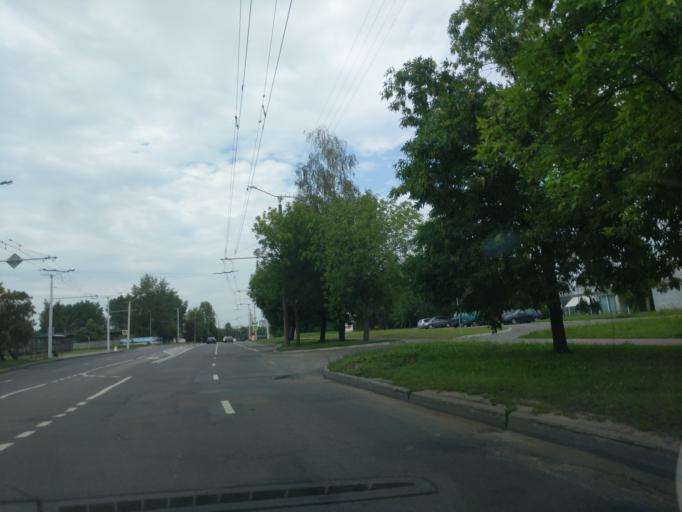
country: BY
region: Minsk
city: Novoye Medvezhino
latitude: 53.8840
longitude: 27.4817
